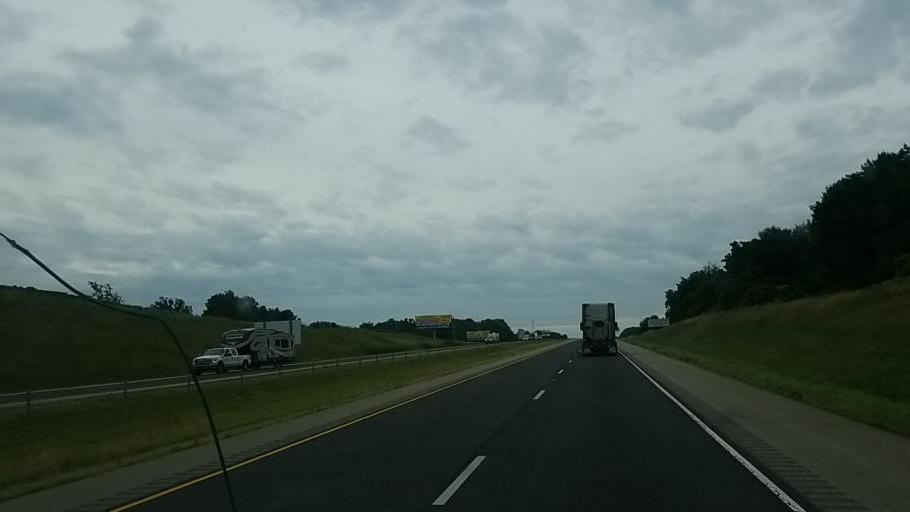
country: US
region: Indiana
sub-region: Steuben County
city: Angola
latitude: 41.6962
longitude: -85.0043
